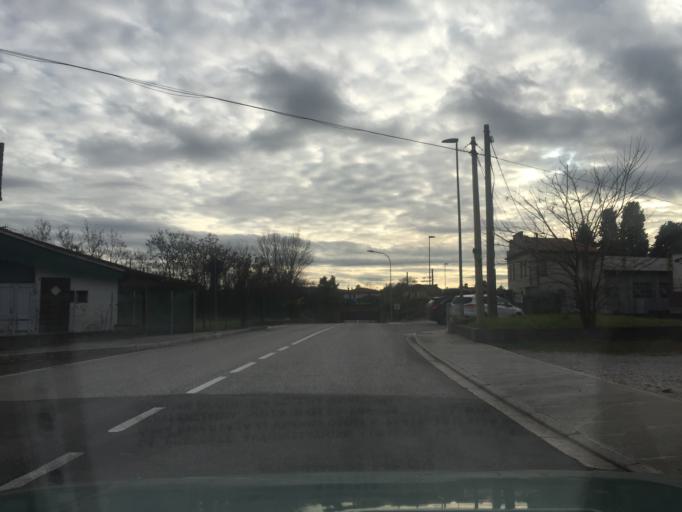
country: IT
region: Friuli Venezia Giulia
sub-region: Provincia di Gorizia
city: Mossa
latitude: 45.9372
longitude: 13.5553
